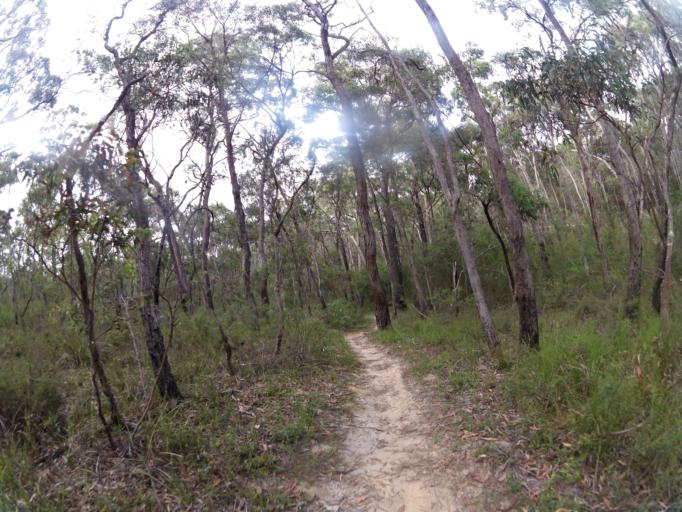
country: AU
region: Victoria
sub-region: Colac-Otway
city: Colac
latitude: -38.4884
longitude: 143.7027
